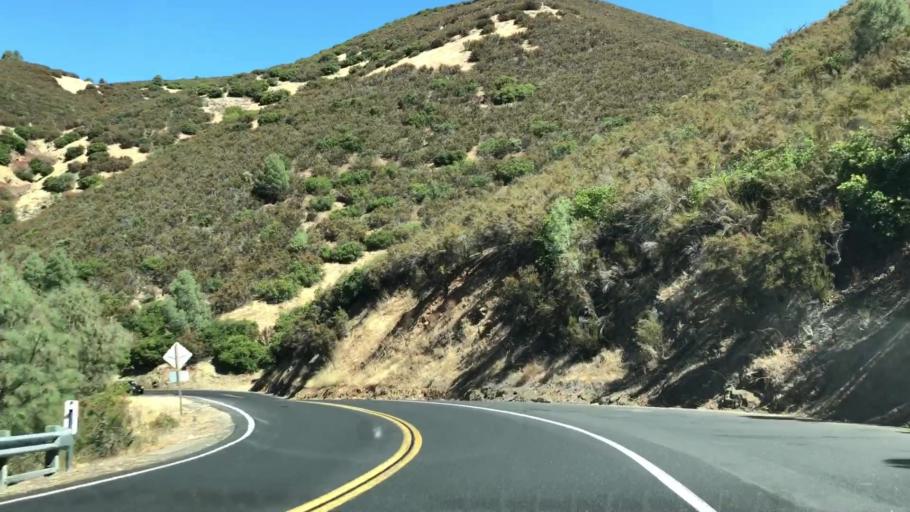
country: US
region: California
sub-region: Tuolumne County
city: Tuolumne City
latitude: 37.8201
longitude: -120.2913
